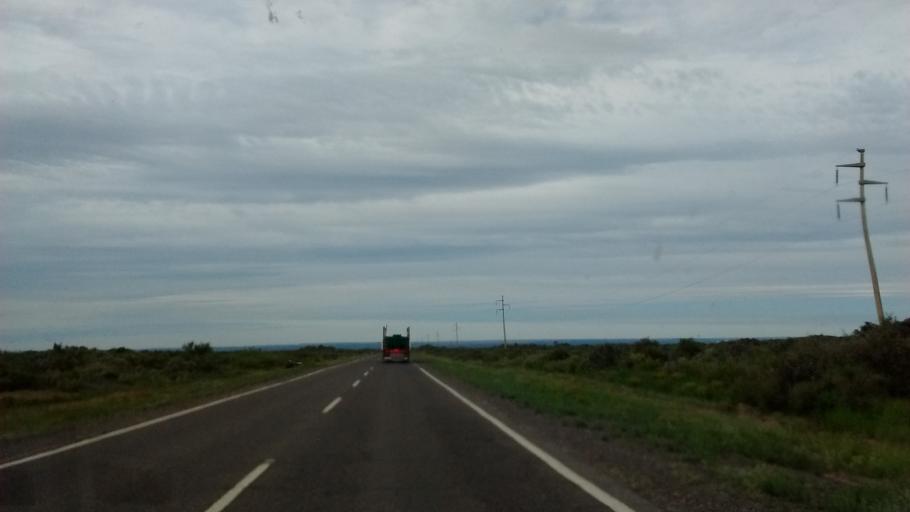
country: AR
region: Rio Negro
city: Catriel
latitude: -37.9543
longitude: -67.8928
